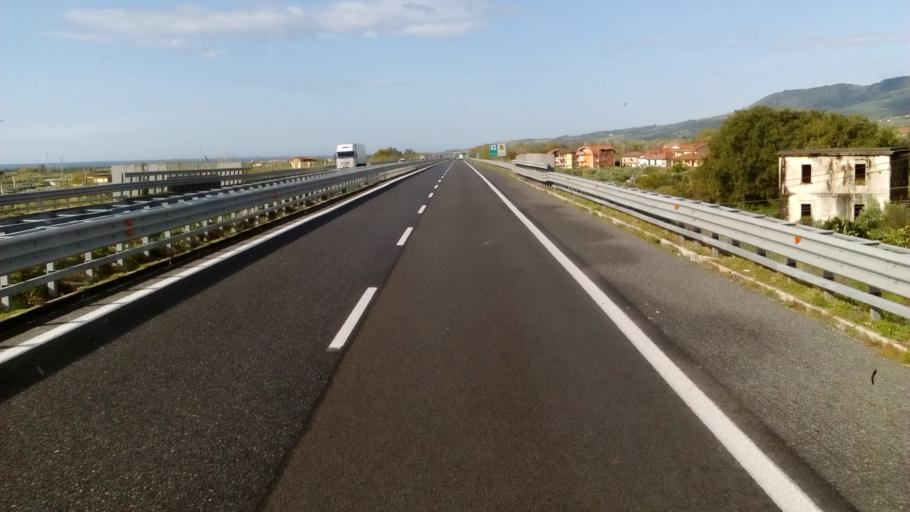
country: IT
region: Calabria
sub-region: Provincia di Catanzaro
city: Santa Eufemia Lamezia
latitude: 38.9260
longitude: 16.2507
